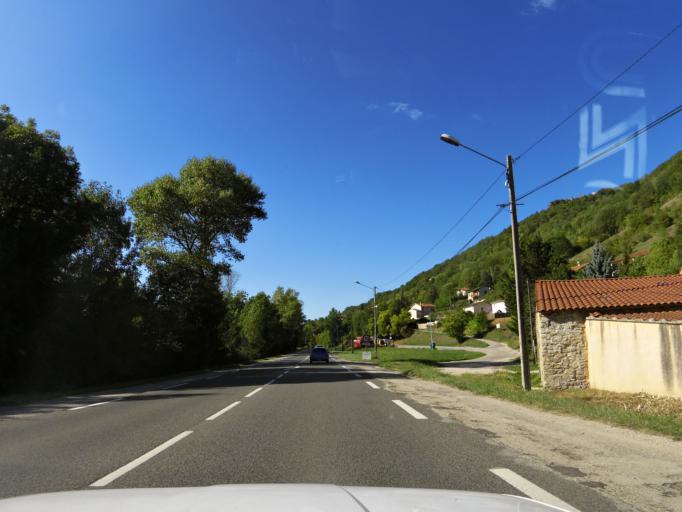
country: FR
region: Rhone-Alpes
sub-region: Departement de l'Ain
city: Vaux-en-Bugey
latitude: 45.9415
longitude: 5.3759
